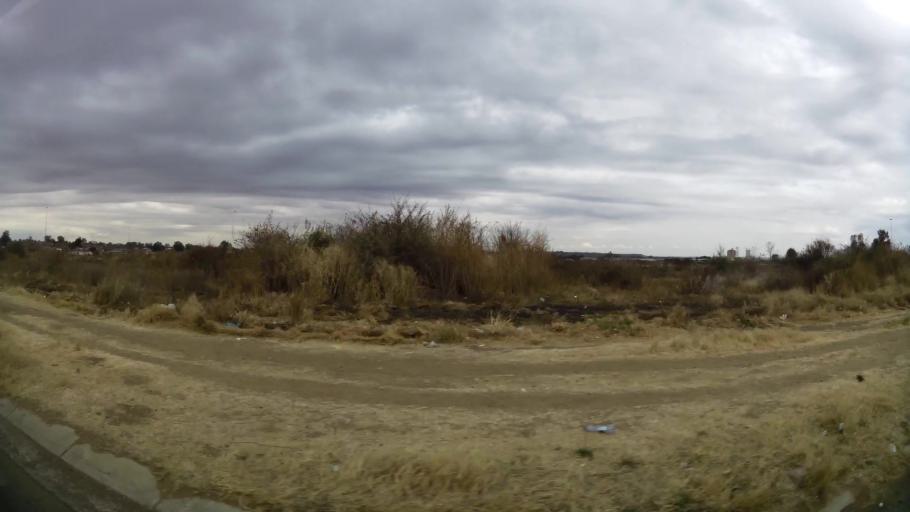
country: ZA
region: Orange Free State
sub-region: Fezile Dabi District Municipality
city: Kroonstad
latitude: -27.6514
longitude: 27.2132
